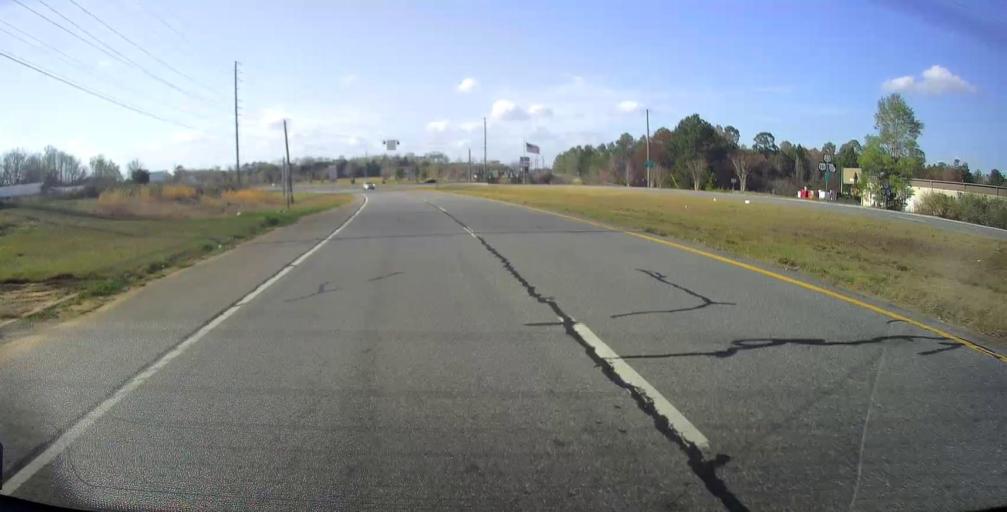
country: US
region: Georgia
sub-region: Dodge County
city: Eastman
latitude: 32.1733
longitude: -83.1599
